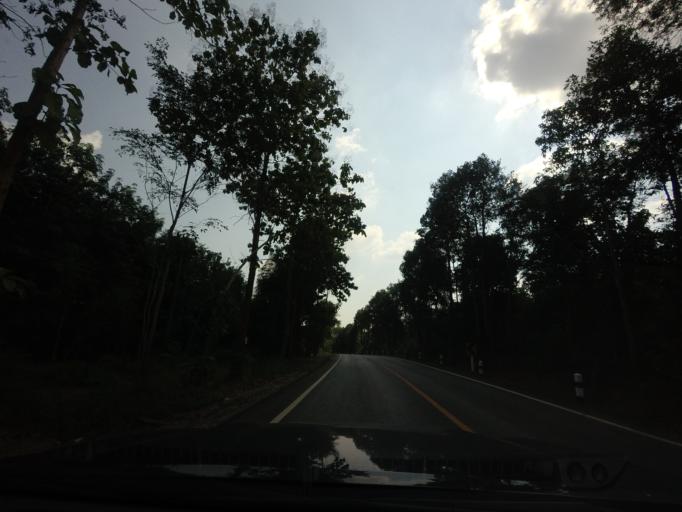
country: TH
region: Nan
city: Santi Suk
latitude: 18.9758
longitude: 100.9292
